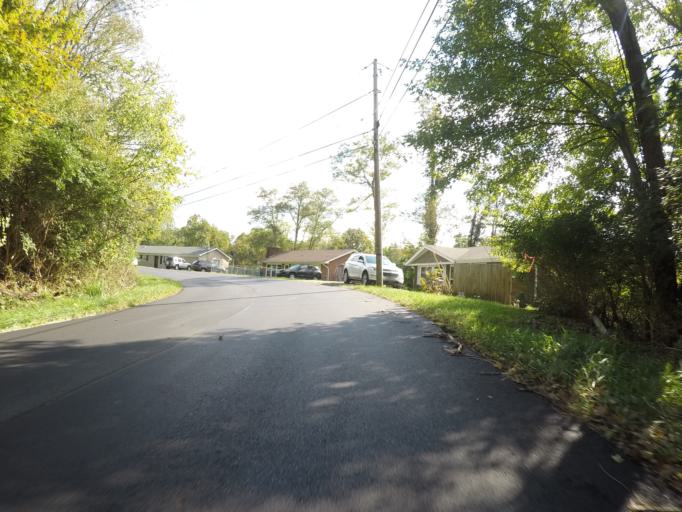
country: US
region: West Virginia
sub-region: Cabell County
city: Huntington
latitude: 38.3816
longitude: -82.4270
